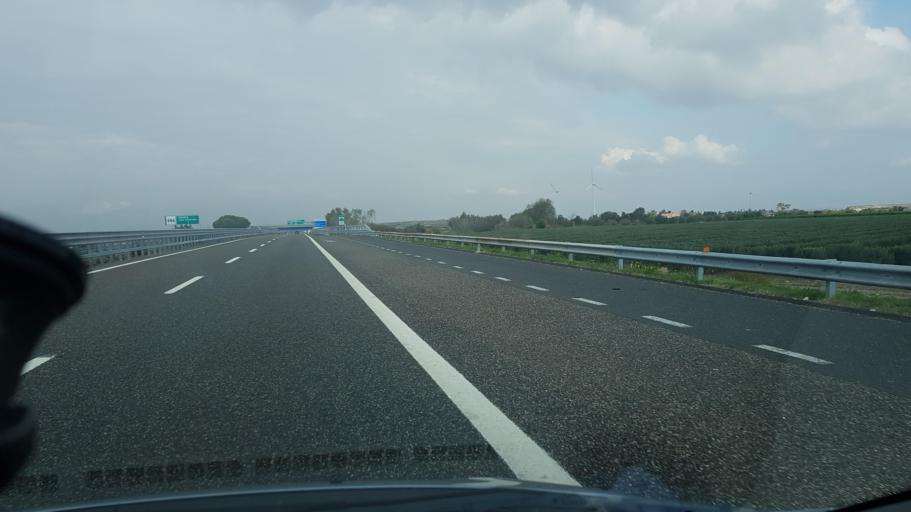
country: IT
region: Apulia
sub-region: Provincia di Foggia
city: Carapelle
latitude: 41.4203
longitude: 15.6632
